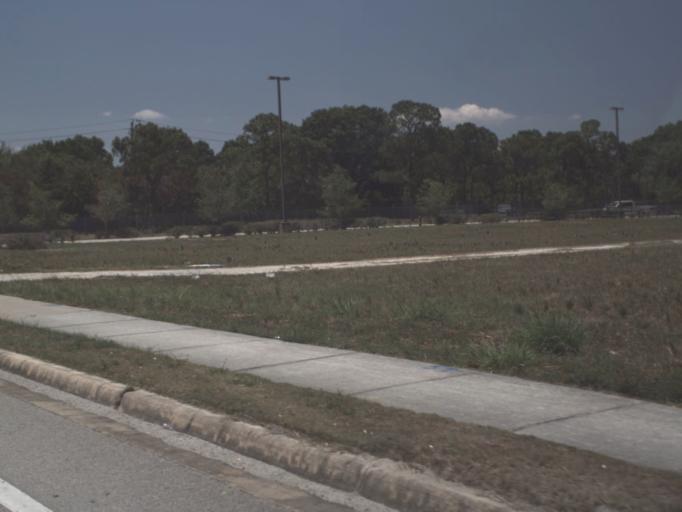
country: US
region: Florida
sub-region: Brevard County
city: June Park
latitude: 28.0790
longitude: -80.6832
